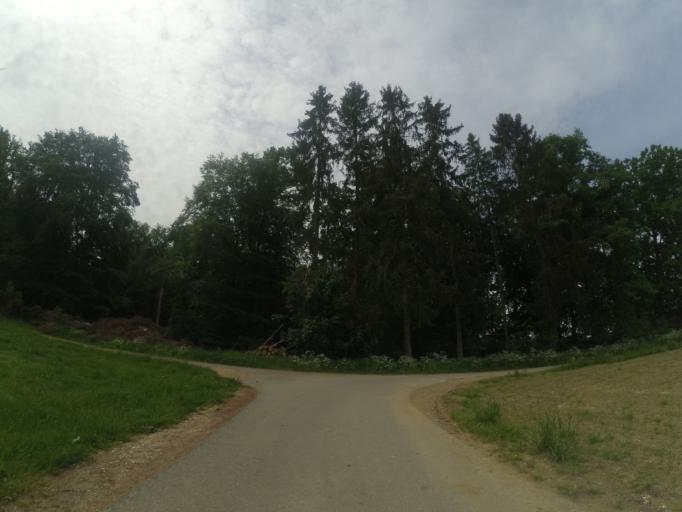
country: DE
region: Baden-Wuerttemberg
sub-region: Tuebingen Region
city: Erbach
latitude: 48.3161
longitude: 9.9231
